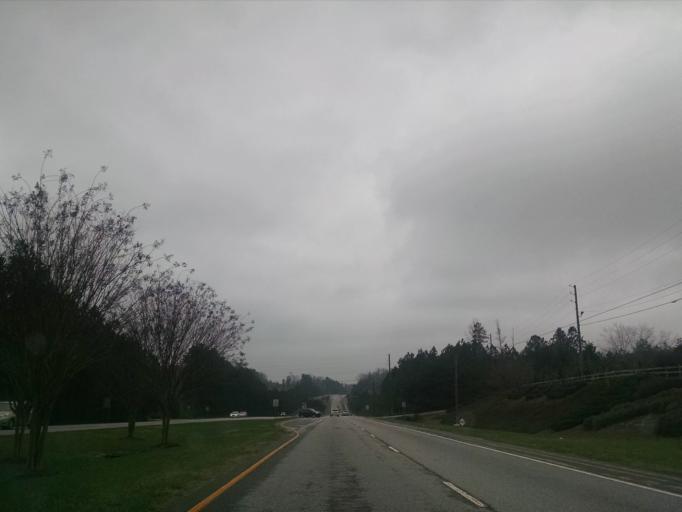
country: US
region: Georgia
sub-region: Gwinnett County
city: Sugar Hill
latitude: 34.0977
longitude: -84.0379
